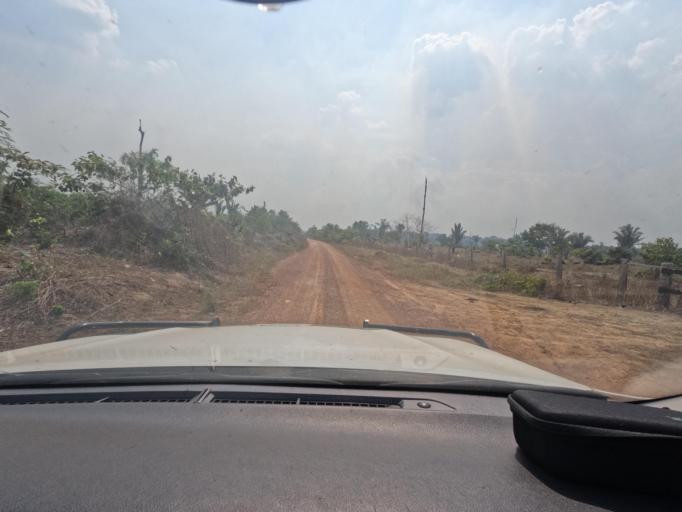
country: BR
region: Rondonia
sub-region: Porto Velho
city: Porto Velho
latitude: -8.7728
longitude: -63.1733
